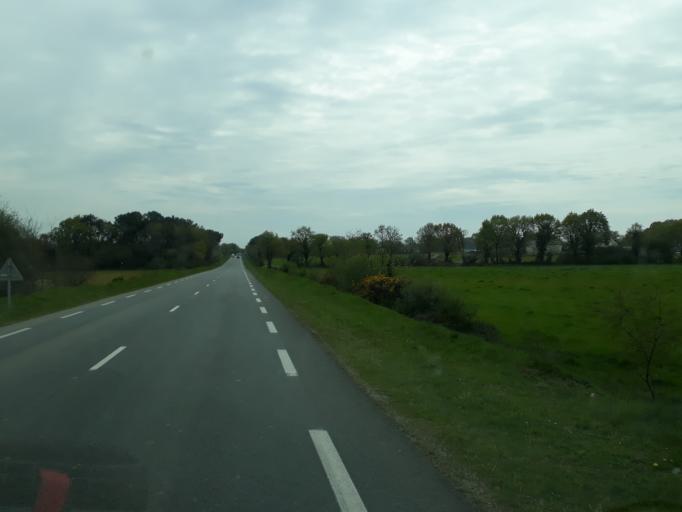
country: FR
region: Brittany
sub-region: Departement du Morbihan
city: Ferel
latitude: 47.5247
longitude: -2.3792
